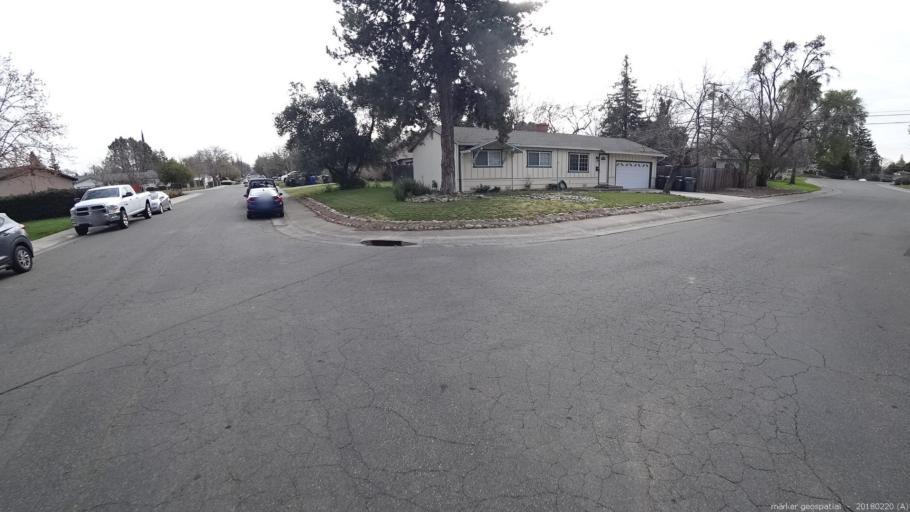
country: US
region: California
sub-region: Sacramento County
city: Orangevale
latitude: 38.6699
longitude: -121.2288
